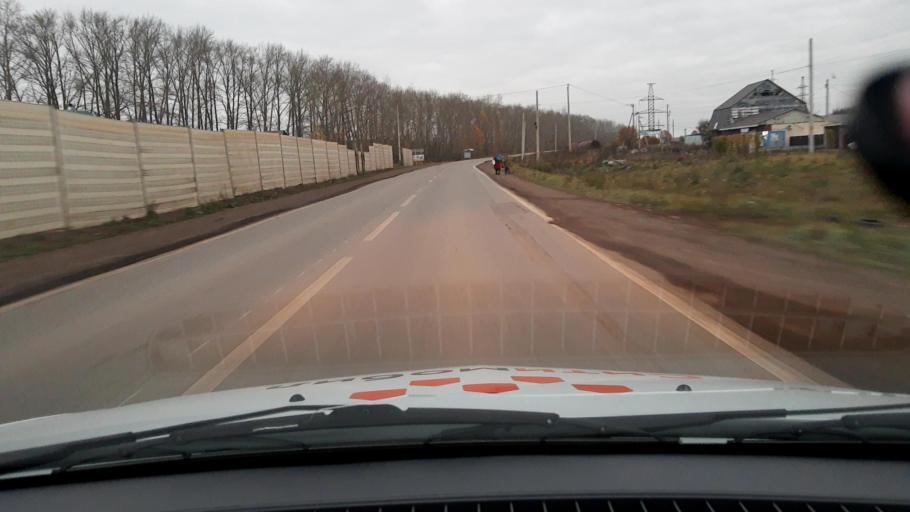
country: RU
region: Bashkortostan
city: Ufa
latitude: 54.6771
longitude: 56.0963
